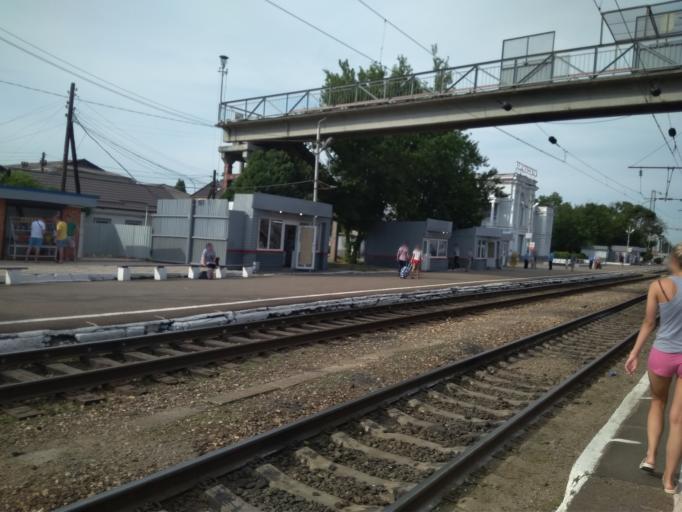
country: RU
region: Krasnodarskiy
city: Belorechensk
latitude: 44.7524
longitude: 39.8931
